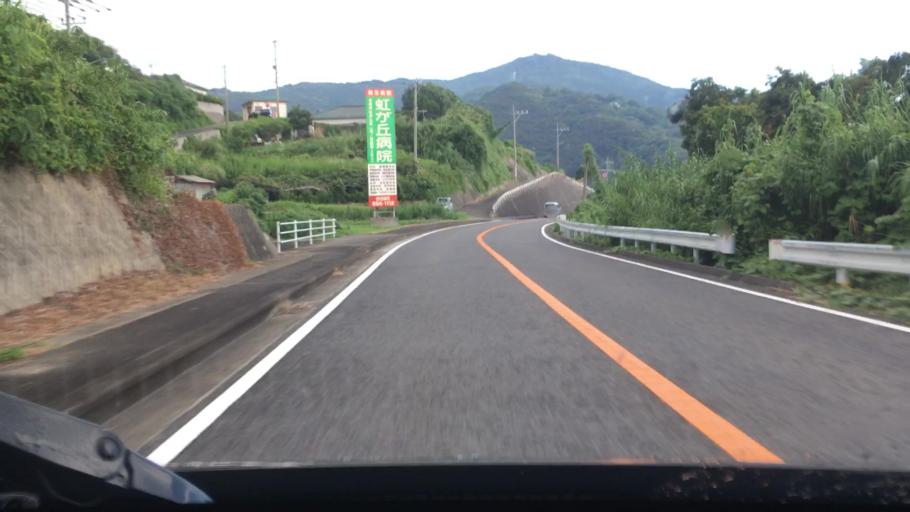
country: JP
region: Nagasaki
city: Togitsu
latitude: 32.8843
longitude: 129.6781
